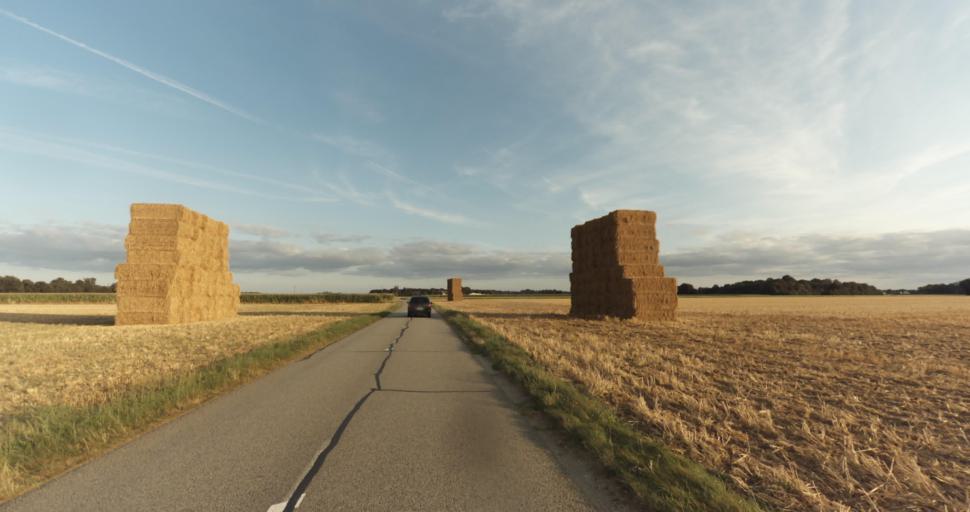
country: FR
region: Haute-Normandie
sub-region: Departement de l'Eure
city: Saint-Germain-sur-Avre
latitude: 48.8508
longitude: 1.2491
